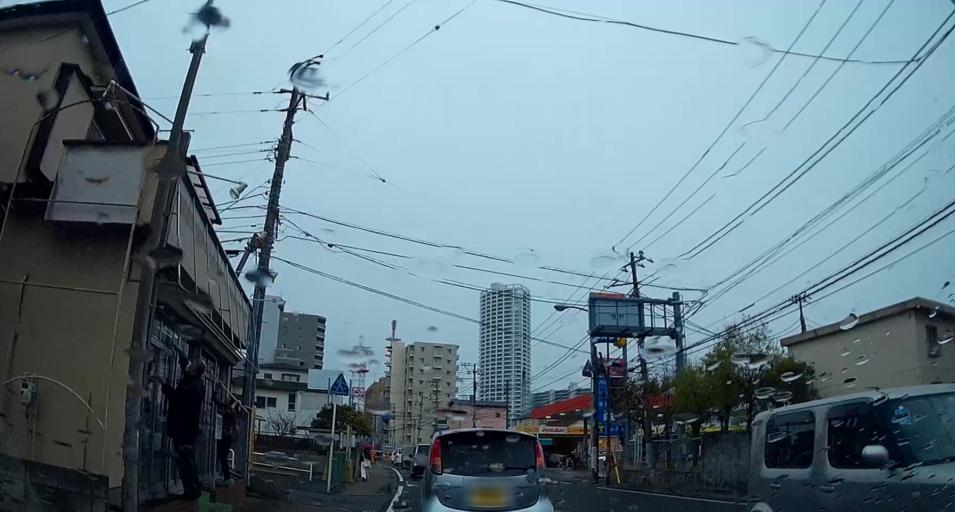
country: JP
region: Chiba
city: Funabashi
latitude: 35.6989
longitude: 139.9776
